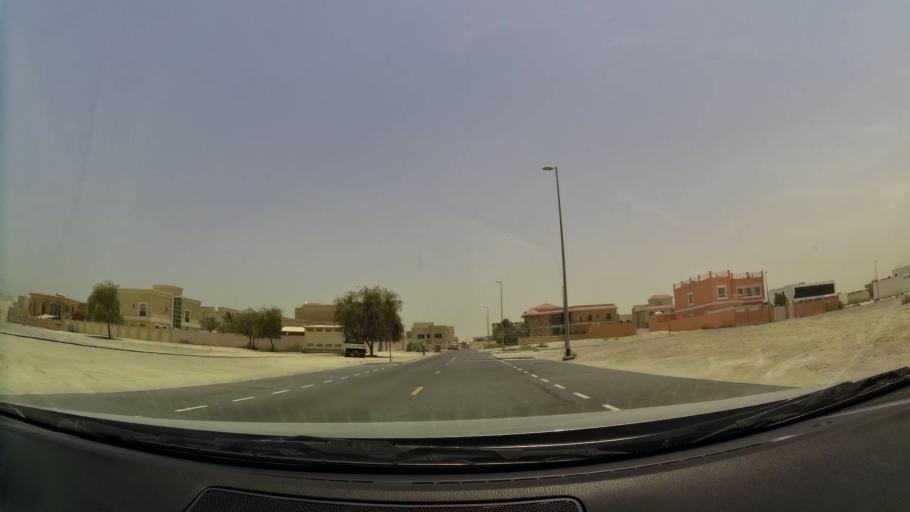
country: AE
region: Dubai
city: Dubai
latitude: 25.0934
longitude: 55.2364
